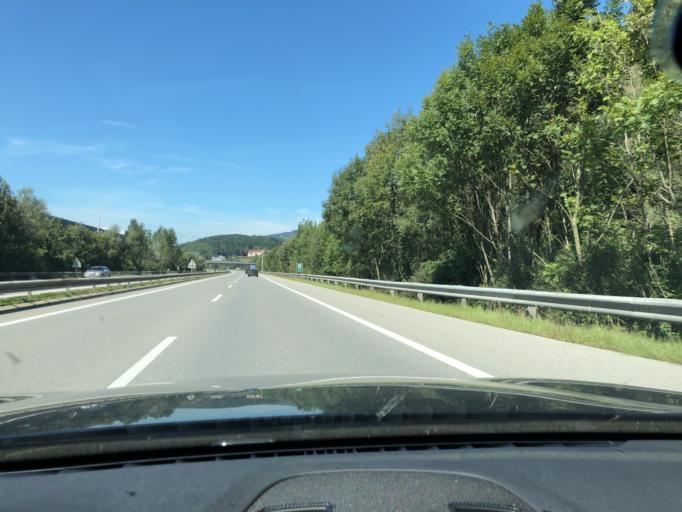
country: AT
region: Vorarlberg
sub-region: Politischer Bezirk Bludenz
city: Nenzing
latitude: 47.1872
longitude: 9.7218
